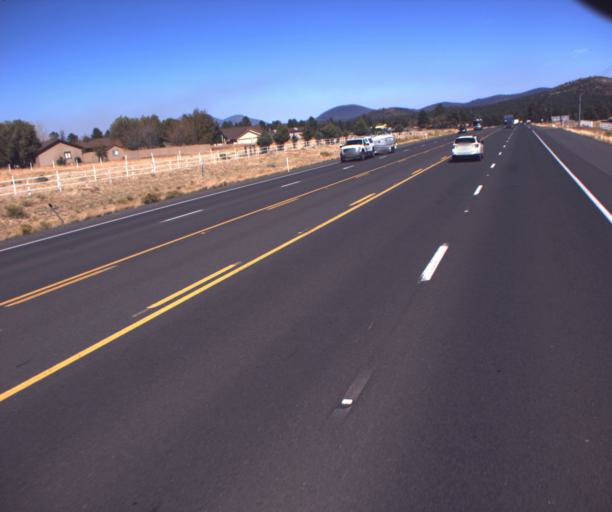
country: US
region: Arizona
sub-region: Coconino County
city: Flagstaff
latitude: 35.2577
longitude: -111.5528
